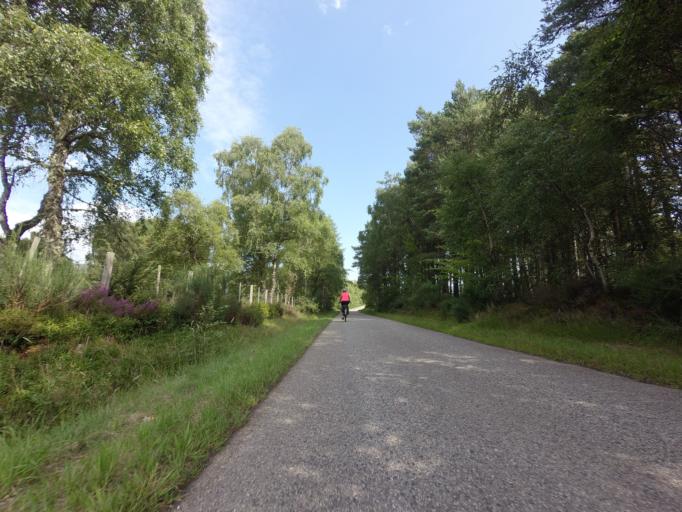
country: GB
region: Scotland
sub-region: Highland
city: Invergordon
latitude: 57.7328
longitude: -4.1912
